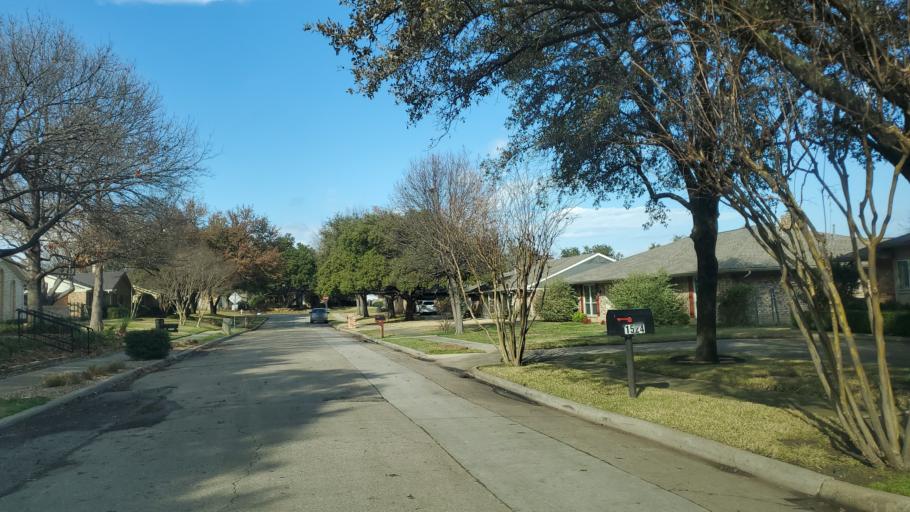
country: US
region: Texas
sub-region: Dallas County
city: Carrollton
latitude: 32.9783
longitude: -96.8986
